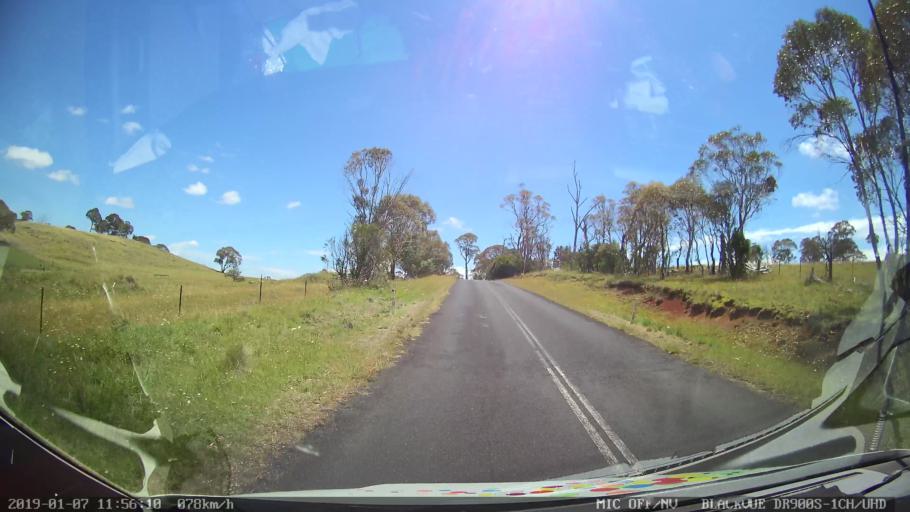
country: AU
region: New South Wales
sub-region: Guyra
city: Guyra
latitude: -30.2776
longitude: 151.6740
